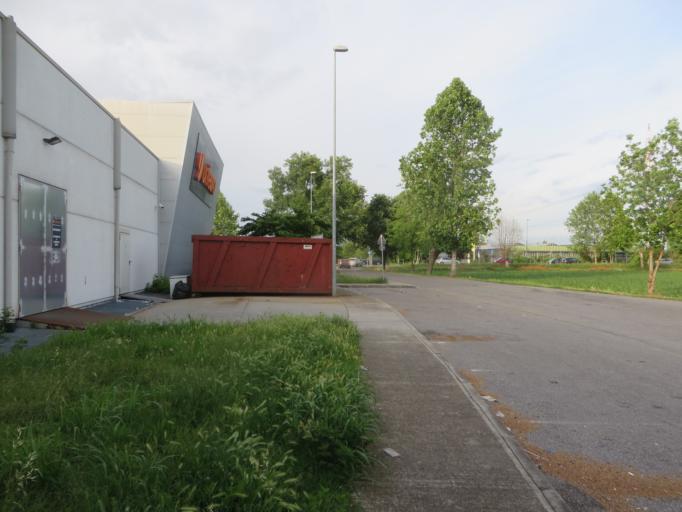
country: IT
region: Lombardy
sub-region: Provincia di Brescia
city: Buffalora-Bettole
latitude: 45.4908
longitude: 10.2736
